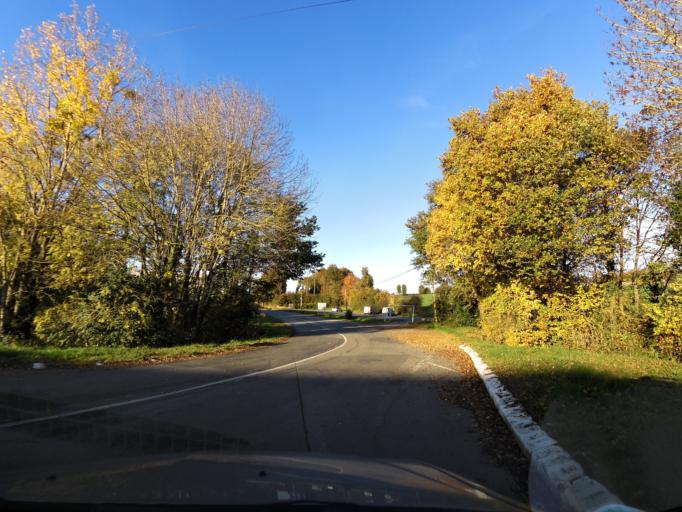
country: FR
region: Brittany
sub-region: Departement d'Ille-et-Vilaine
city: Pance
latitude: 47.8930
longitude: -1.6857
